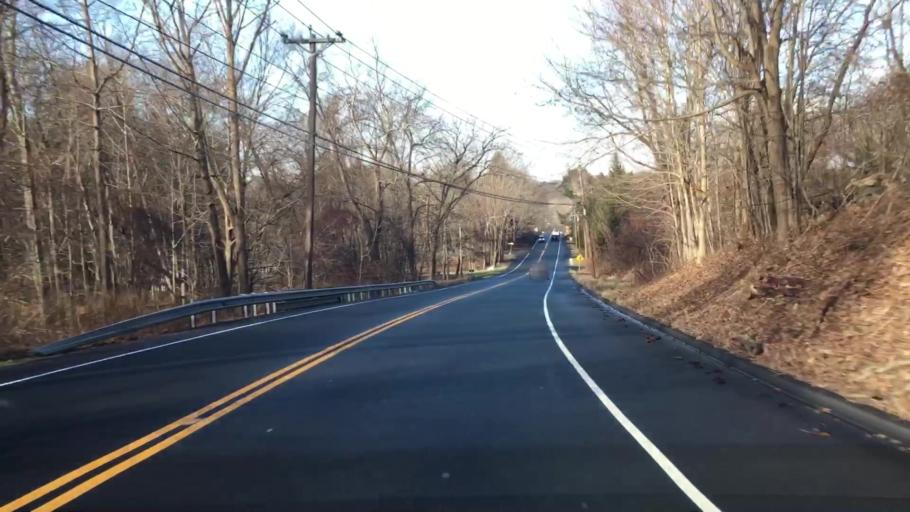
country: US
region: Connecticut
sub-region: Fairfield County
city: Newtown
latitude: 41.3928
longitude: -73.2275
